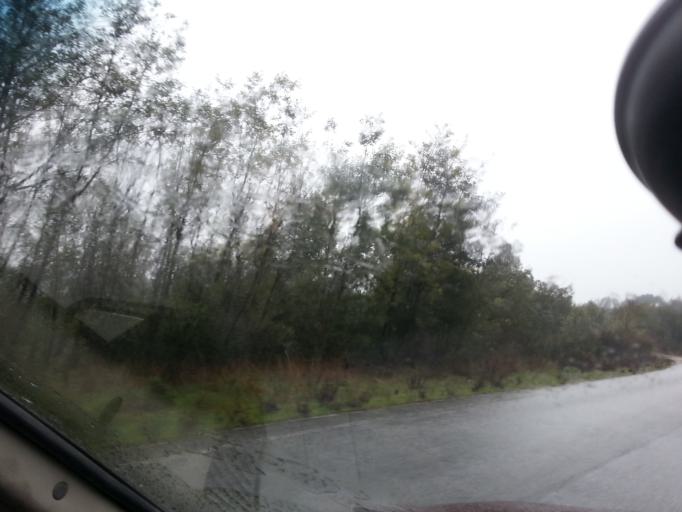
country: PT
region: Guarda
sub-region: Fornos de Algodres
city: Fornos de Algodres
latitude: 40.6083
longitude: -7.5341
